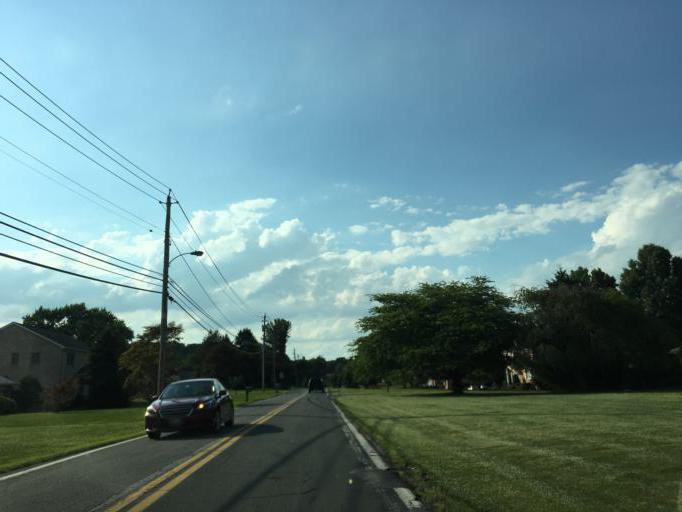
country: US
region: Maryland
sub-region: Baltimore County
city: Kingsville
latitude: 39.4378
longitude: -76.4352
